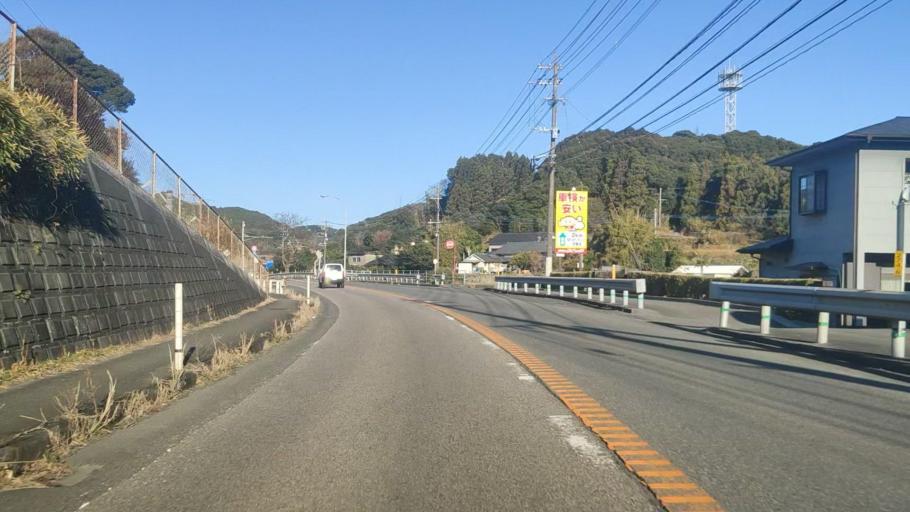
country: JP
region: Miyazaki
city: Nobeoka
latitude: 32.3760
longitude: 131.6298
